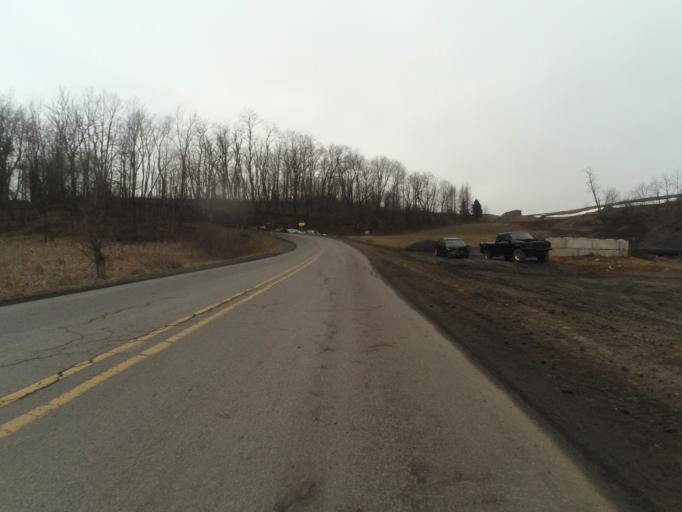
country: US
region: Pennsylvania
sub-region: Centre County
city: Centre Hall
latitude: 40.8133
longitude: -77.6270
